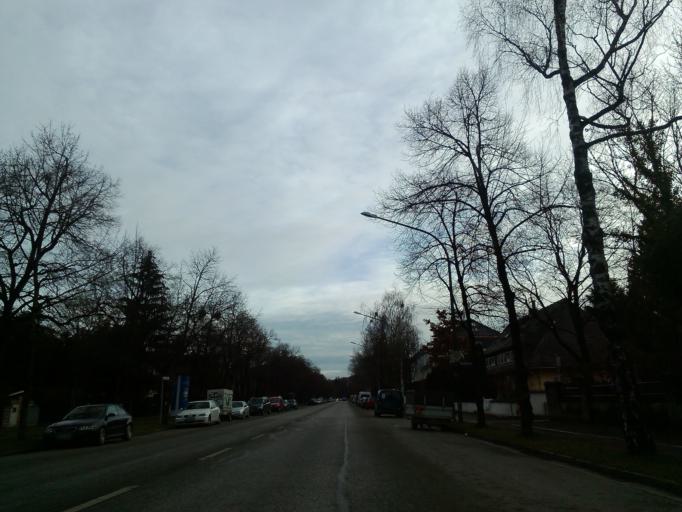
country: DE
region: Bavaria
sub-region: Upper Bavaria
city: Neuried
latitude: 48.1135
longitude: 11.4882
